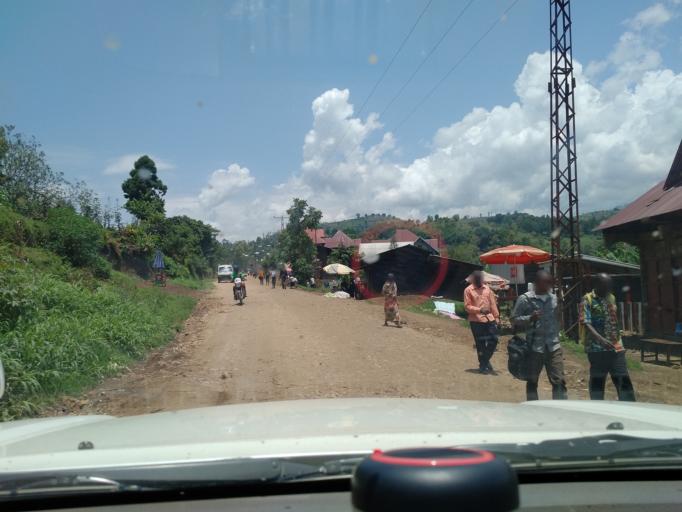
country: CD
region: Nord Kivu
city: Sake
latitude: -1.7111
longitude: 29.0184
